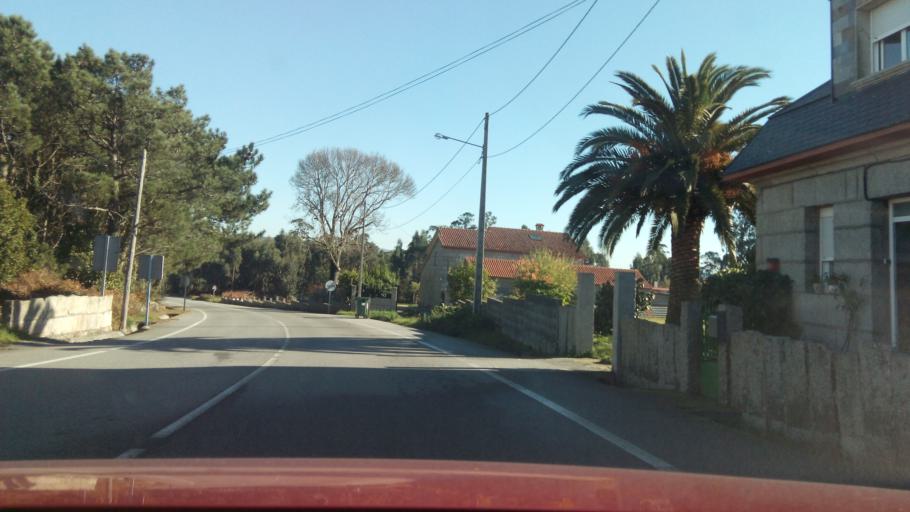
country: ES
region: Galicia
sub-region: Provincia de Pontevedra
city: O Grove
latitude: 42.4679
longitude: -8.9186
